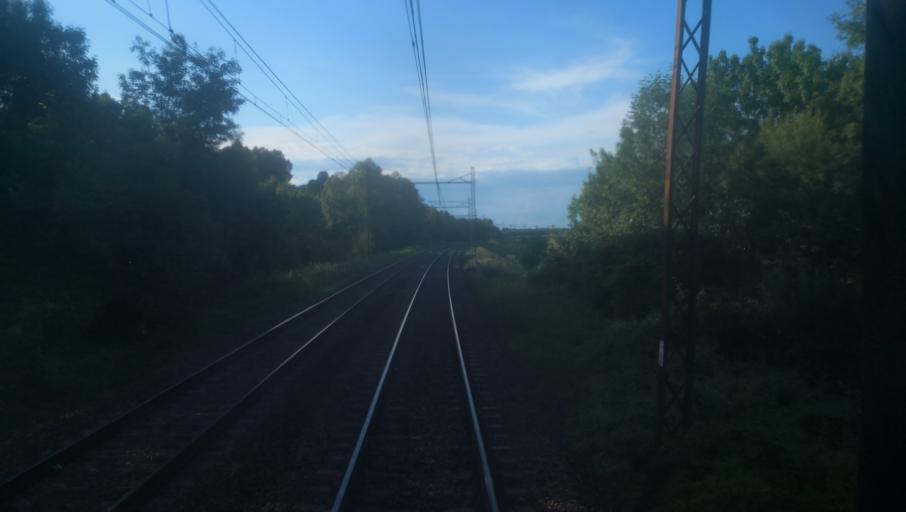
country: FR
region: Centre
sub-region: Departement du Cher
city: Mereau
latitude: 47.1275
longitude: 2.0457
